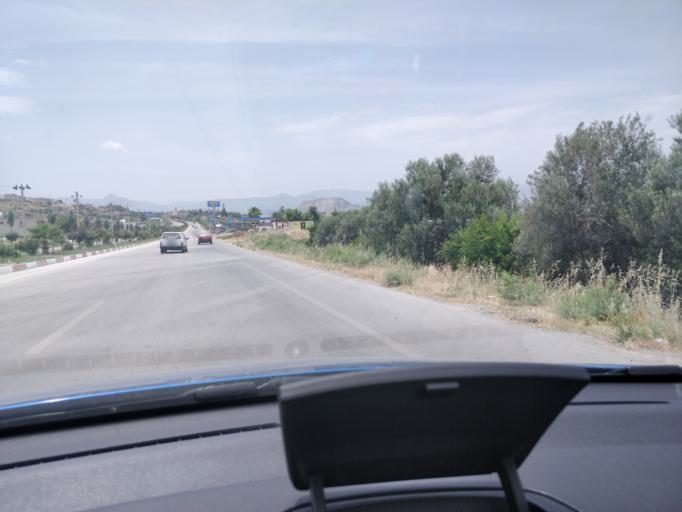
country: TR
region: Mersin
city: Mut
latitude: 36.6247
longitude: 33.4446
